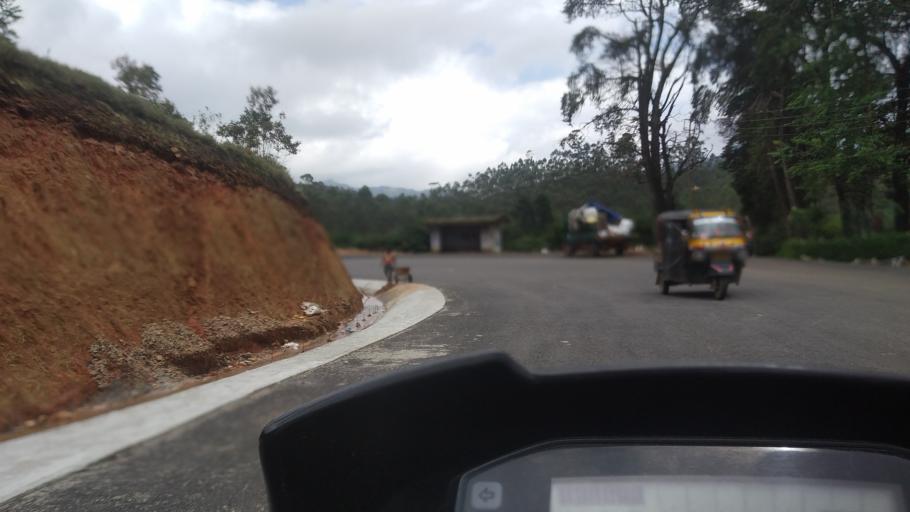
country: IN
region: Kerala
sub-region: Idukki
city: Munnar
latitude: 10.0723
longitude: 77.0924
